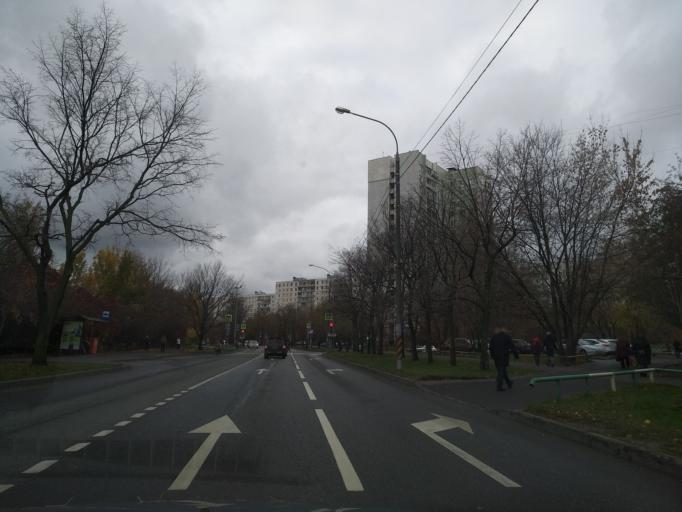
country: RU
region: Moscow
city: Bibirevo
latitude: 55.8865
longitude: 37.6026
